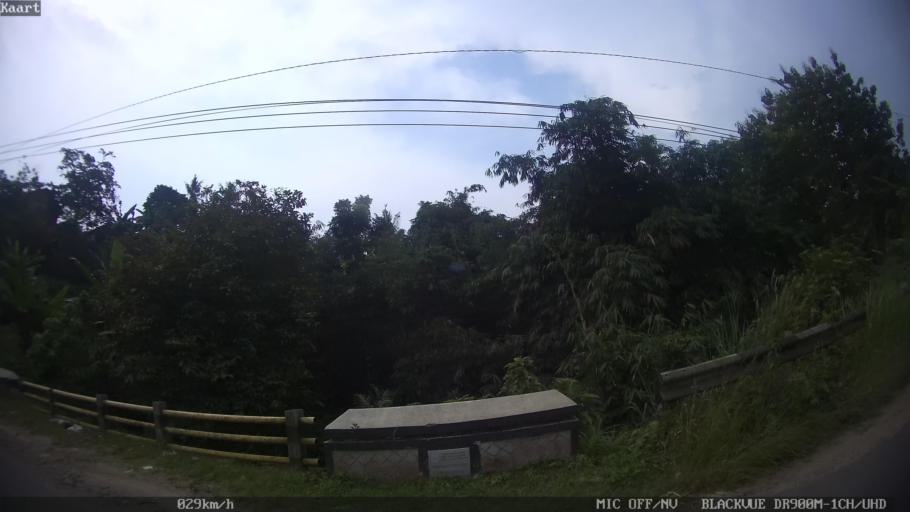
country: ID
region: Lampung
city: Bandarlampung
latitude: -5.4218
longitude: 105.2857
